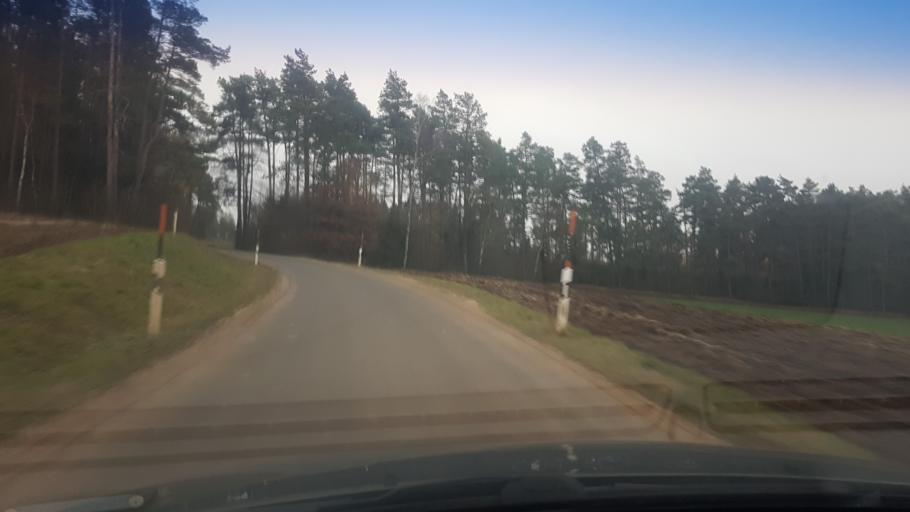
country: DE
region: Bavaria
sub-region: Upper Franconia
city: Weismain
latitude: 50.0429
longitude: 11.2873
